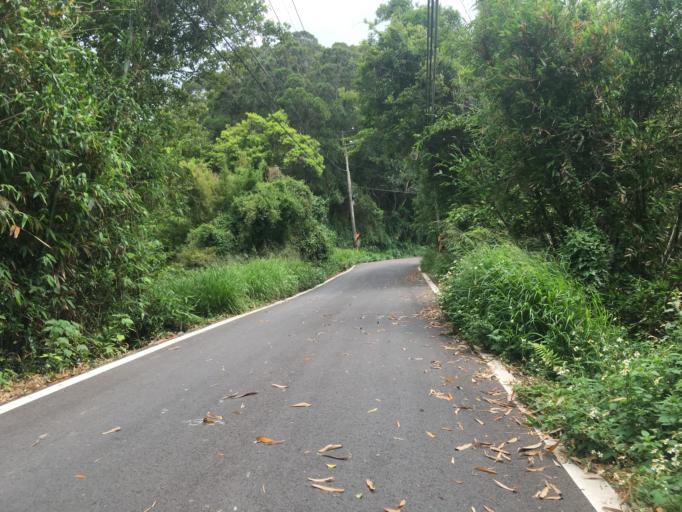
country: TW
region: Taiwan
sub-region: Hsinchu
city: Hsinchu
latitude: 24.7457
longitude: 120.9847
